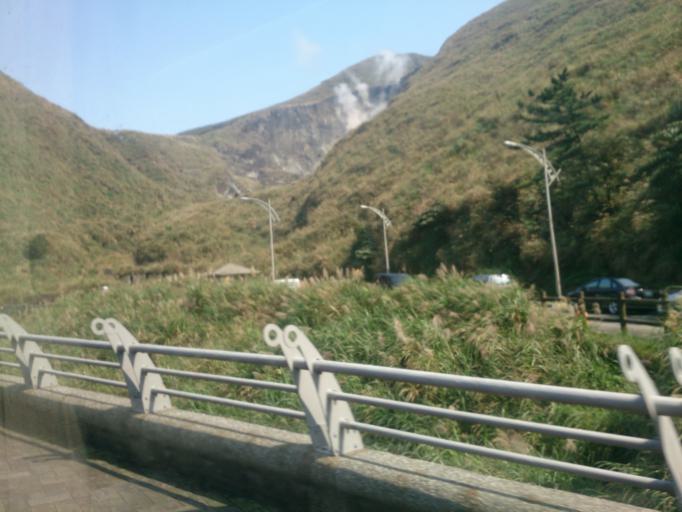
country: TW
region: Taipei
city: Taipei
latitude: 25.1758
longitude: 121.5440
